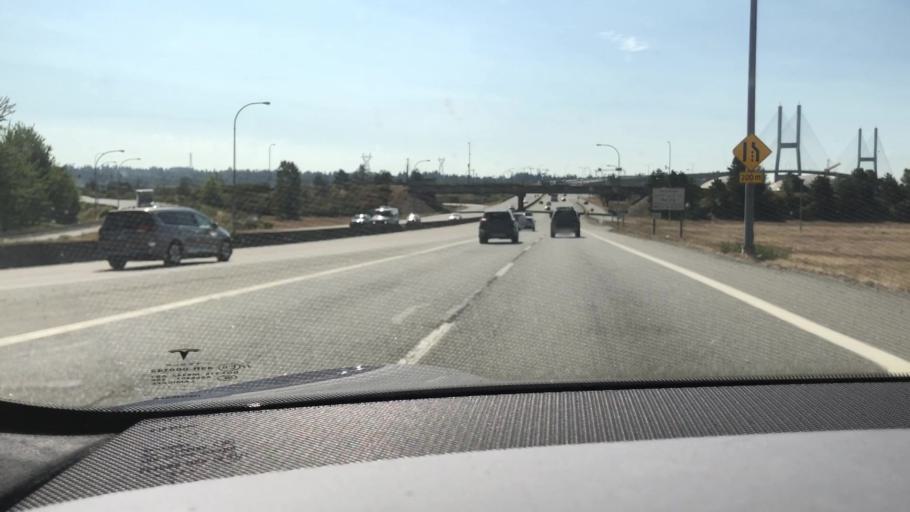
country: CA
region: British Columbia
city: Delta
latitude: 49.1724
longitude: -122.9540
